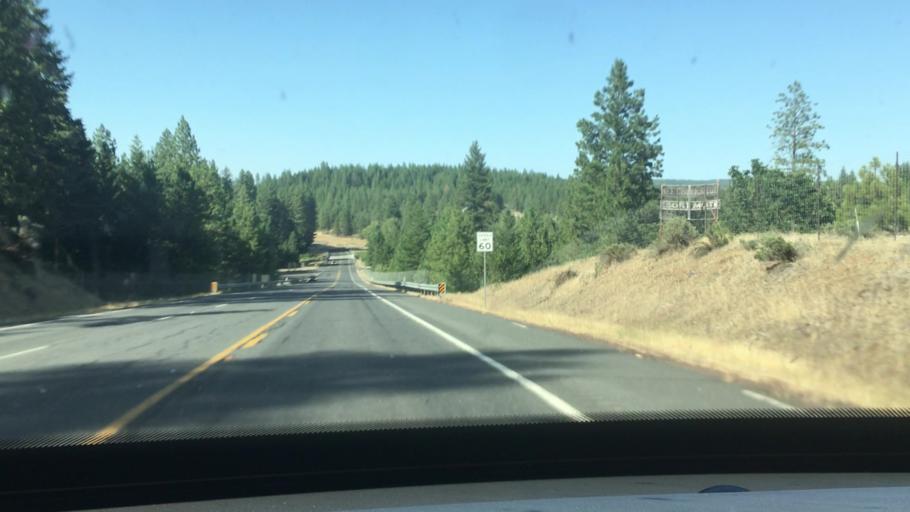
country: US
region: Washington
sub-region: Klickitat County
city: Goldendale
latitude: 45.9107
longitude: -120.7092
